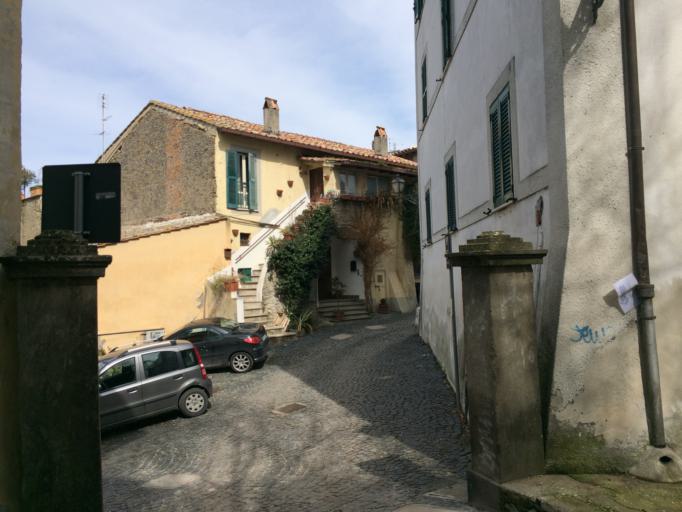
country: IT
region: Latium
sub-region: Citta metropolitana di Roma Capitale
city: Anguillara Sabazia
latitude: 42.0929
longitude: 12.2704
